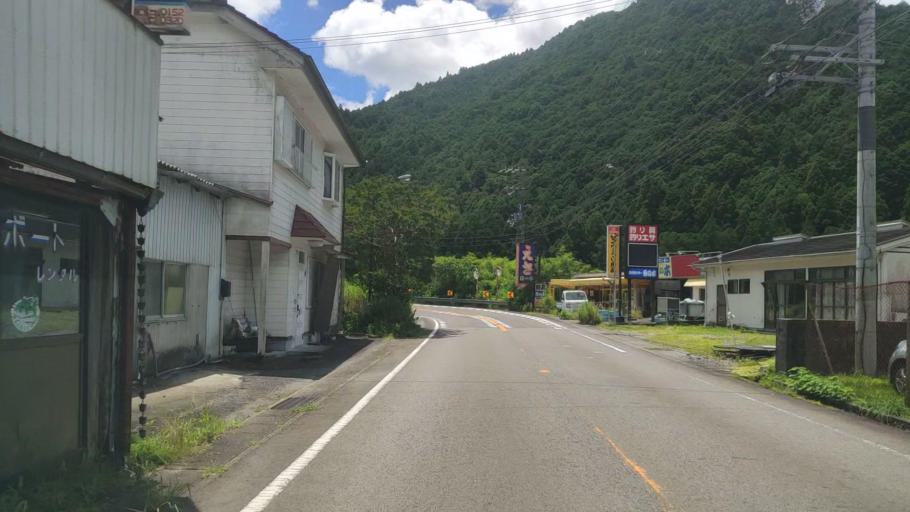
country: JP
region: Mie
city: Owase
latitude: 33.9639
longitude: 136.0608
